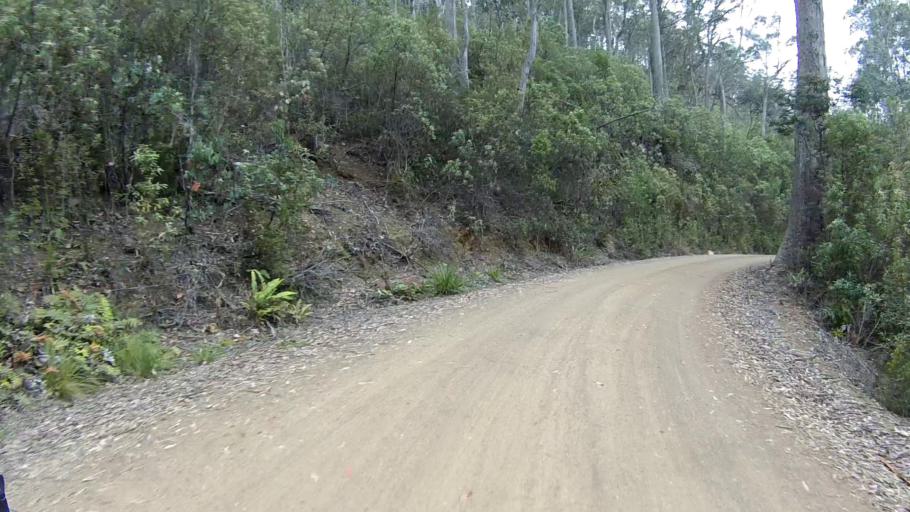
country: AU
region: Tasmania
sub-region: Sorell
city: Sorell
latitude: -42.6068
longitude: 147.8778
